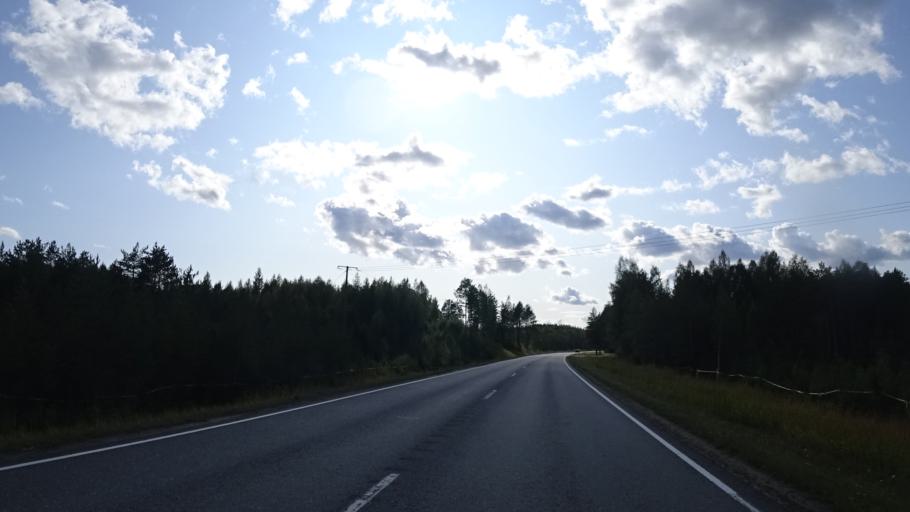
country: FI
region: North Karelia
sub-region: Keski-Karjala
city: Kitee
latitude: 62.0958
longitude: 30.1024
